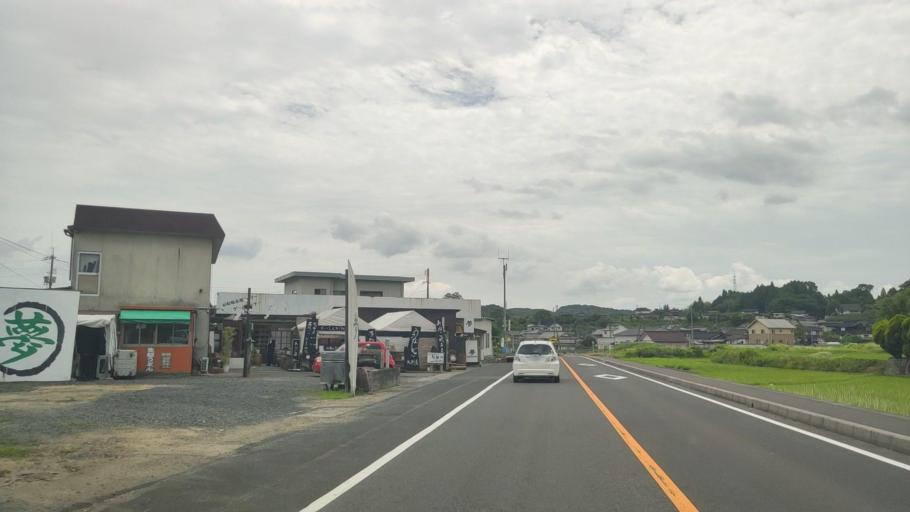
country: JP
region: Okayama
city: Tsuyama
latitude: 35.0602
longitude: 133.8875
